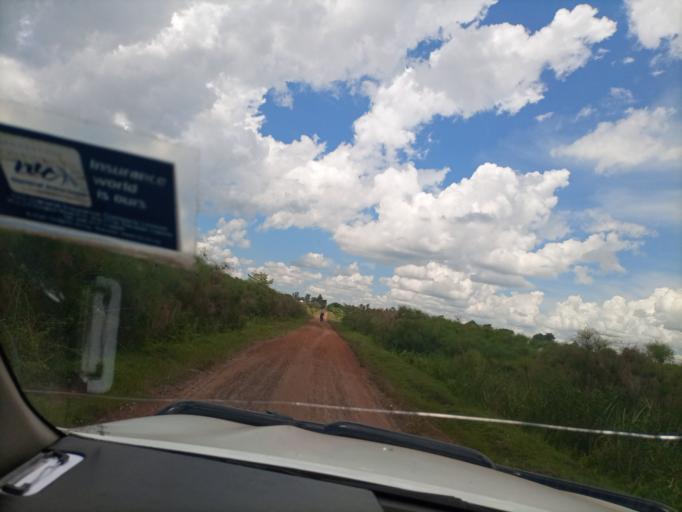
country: UG
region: Eastern Region
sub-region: Tororo District
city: Tororo
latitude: 0.6357
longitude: 33.9926
